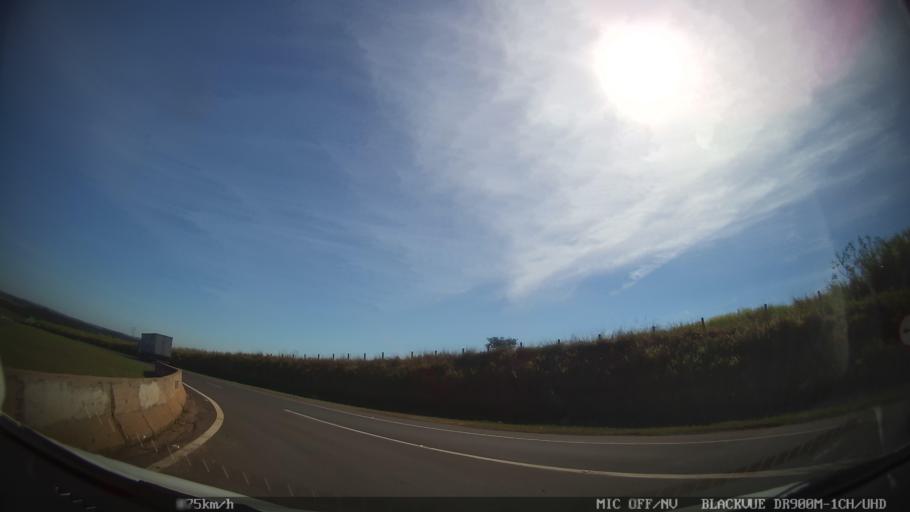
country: BR
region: Sao Paulo
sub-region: Porto Ferreira
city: Porto Ferreira
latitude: -21.8354
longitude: -47.4912
